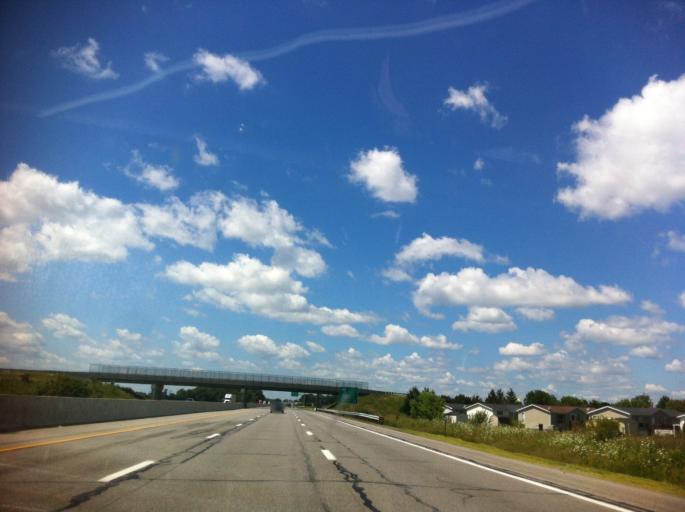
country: US
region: Ohio
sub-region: Wood County
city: Walbridge
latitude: 41.5476
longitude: -83.5362
